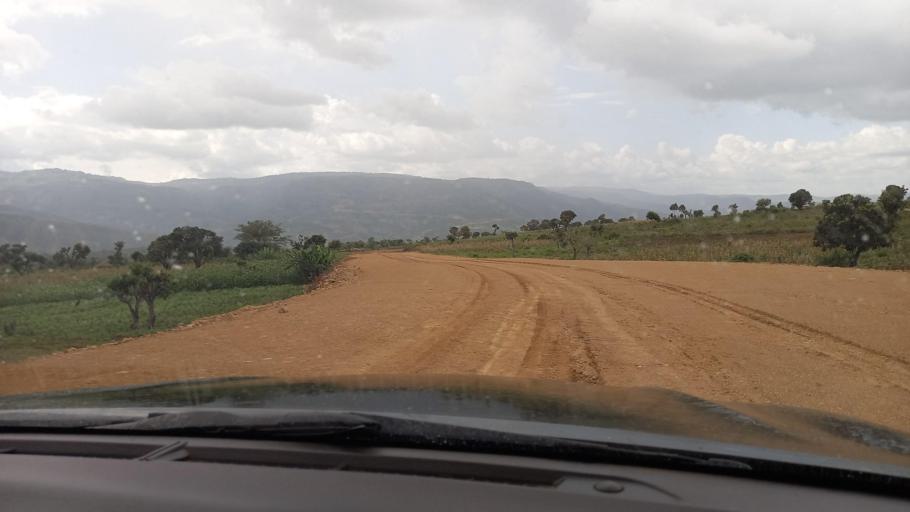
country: ET
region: Southern Nations, Nationalities, and People's Region
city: Mizan Teferi
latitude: 6.1751
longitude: 35.7065
